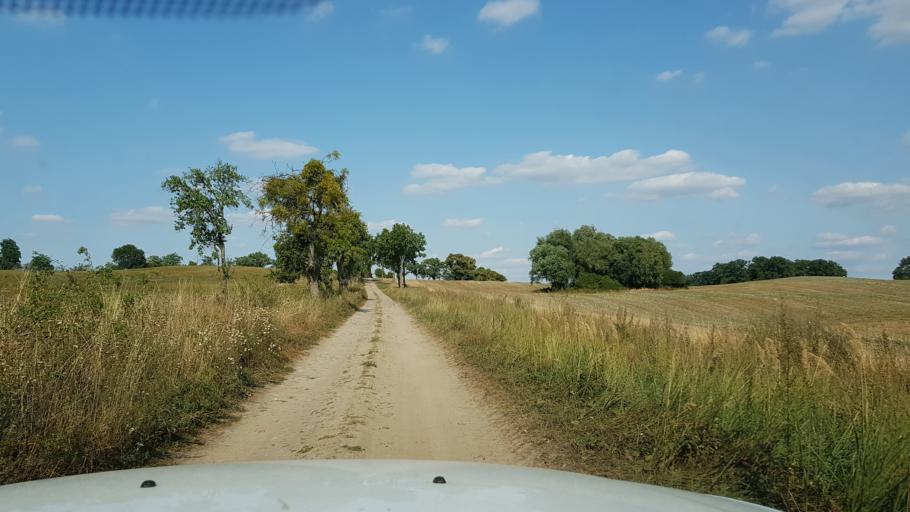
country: PL
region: West Pomeranian Voivodeship
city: Trzcinsko Zdroj
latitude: 52.9031
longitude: 14.5739
